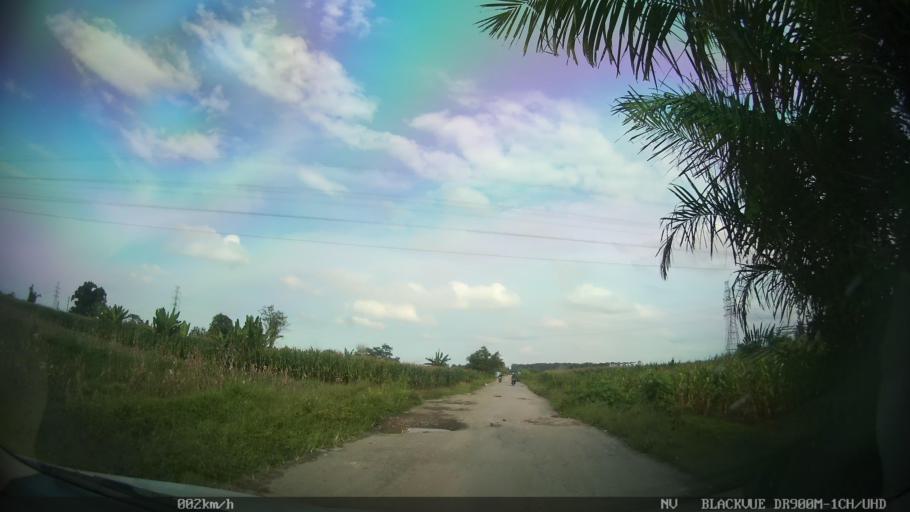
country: ID
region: North Sumatra
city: Percut
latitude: 3.5682
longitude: 98.7823
